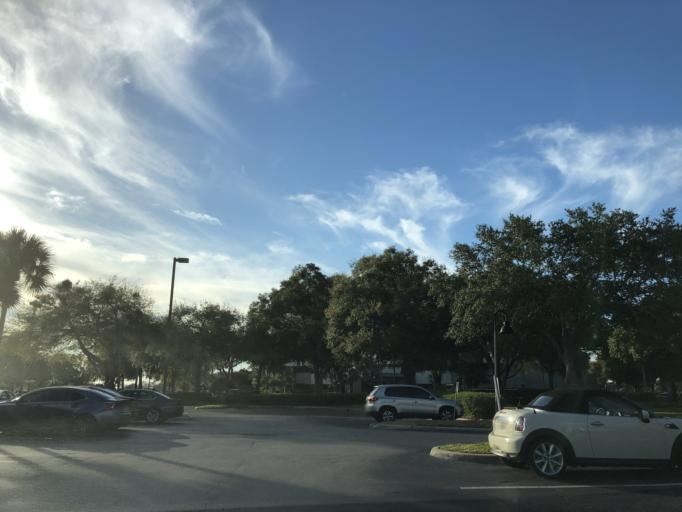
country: US
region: Florida
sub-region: Orange County
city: Doctor Phillips
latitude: 28.4467
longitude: -81.4717
